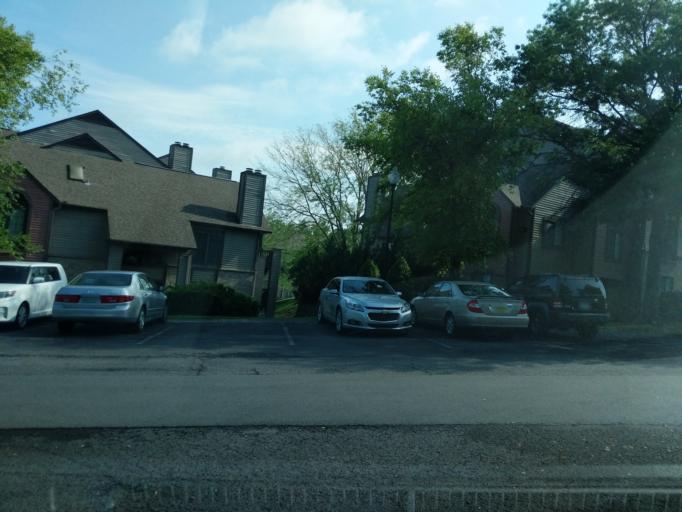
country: US
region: Tennessee
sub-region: Sumner County
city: Hendersonville
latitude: 36.3093
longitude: -86.6548
